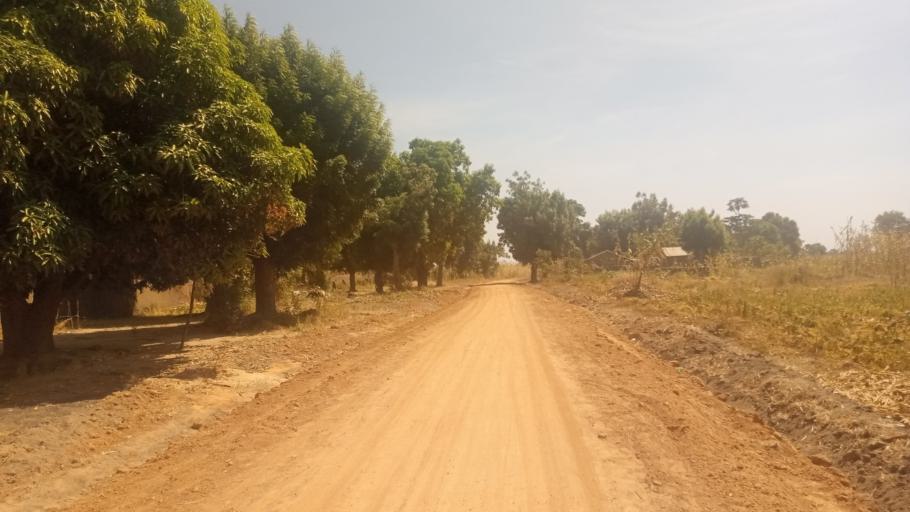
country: NG
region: Adamawa
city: Madagali
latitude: 10.8503
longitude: 13.3916
